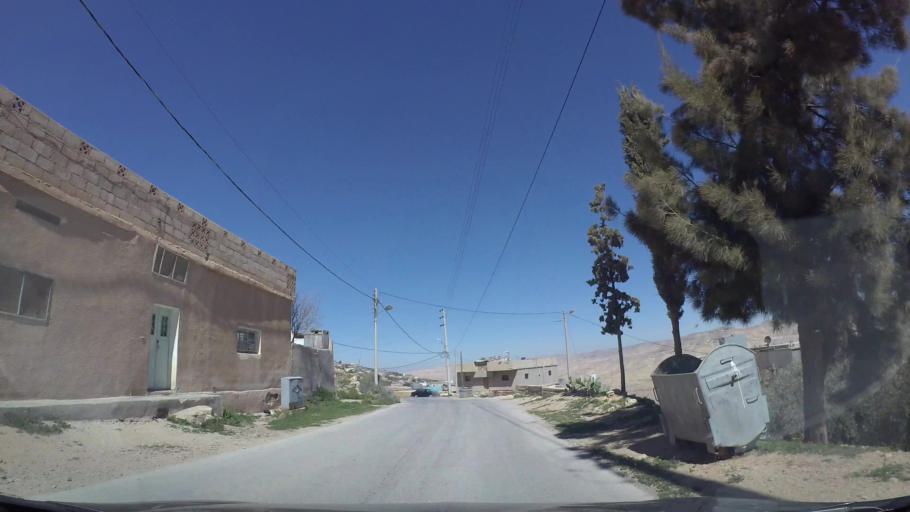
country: JO
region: Tafielah
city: At Tafilah
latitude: 30.8294
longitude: 35.5795
